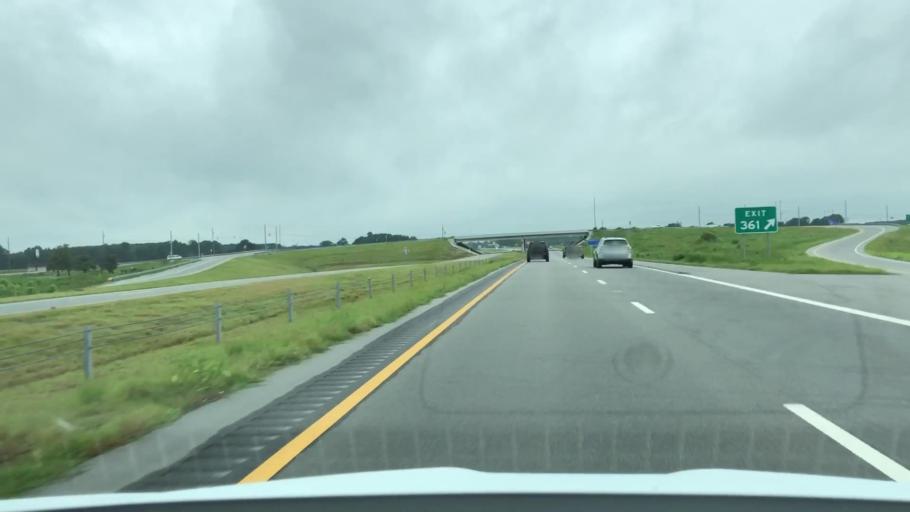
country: US
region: North Carolina
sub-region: Wayne County
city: Elroy
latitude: 35.4106
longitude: -77.8939
